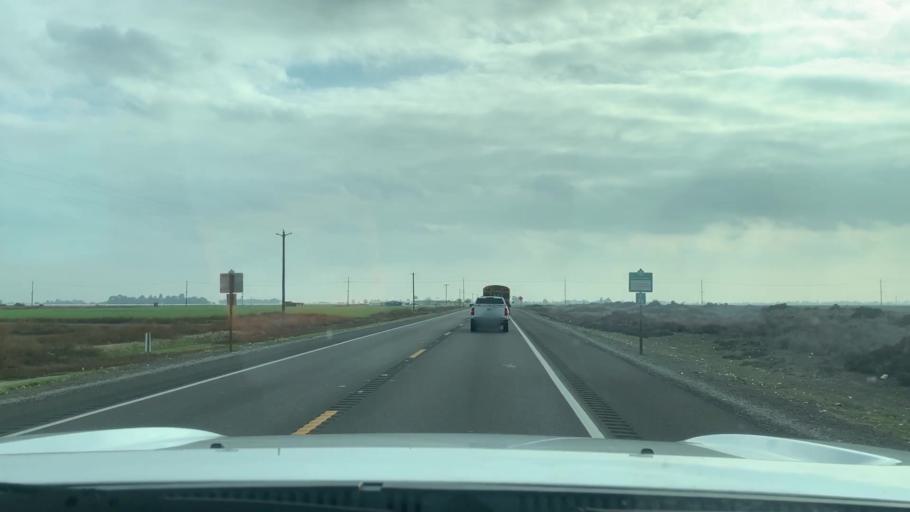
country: US
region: California
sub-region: Kings County
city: Stratford
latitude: 36.2306
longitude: -119.8163
